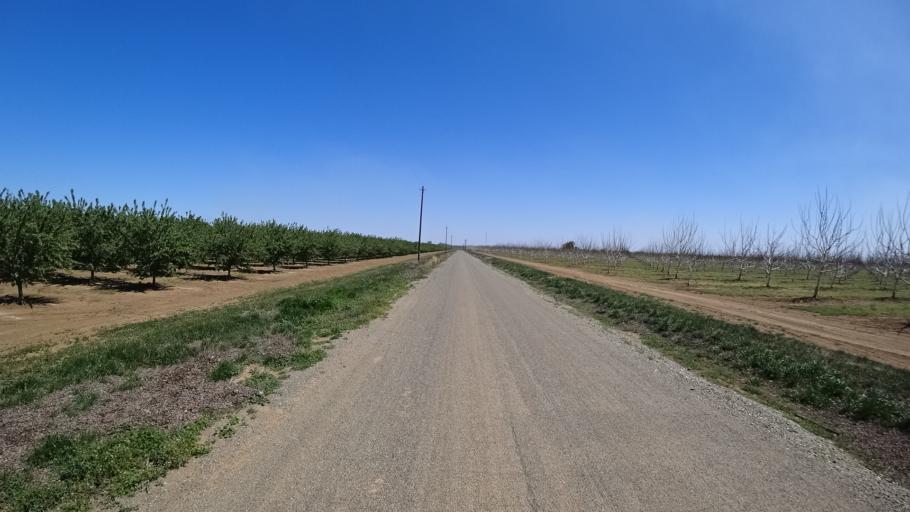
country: US
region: California
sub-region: Glenn County
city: Willows
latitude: 39.4510
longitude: -122.2575
